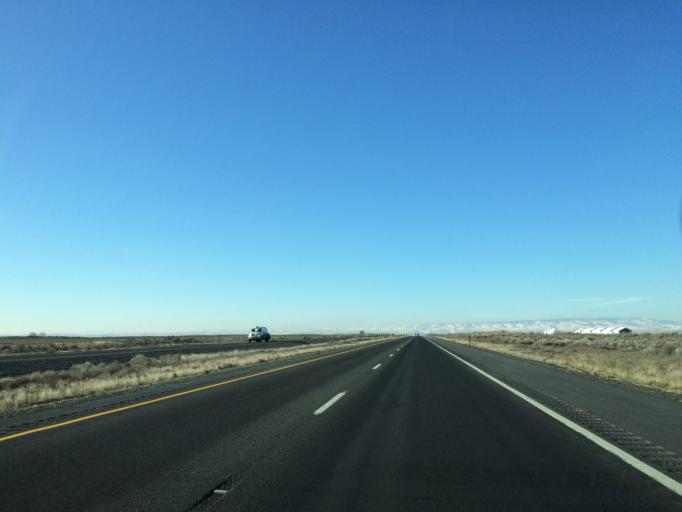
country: US
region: Washington
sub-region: Grant County
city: Royal City
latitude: 47.1040
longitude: -119.6683
